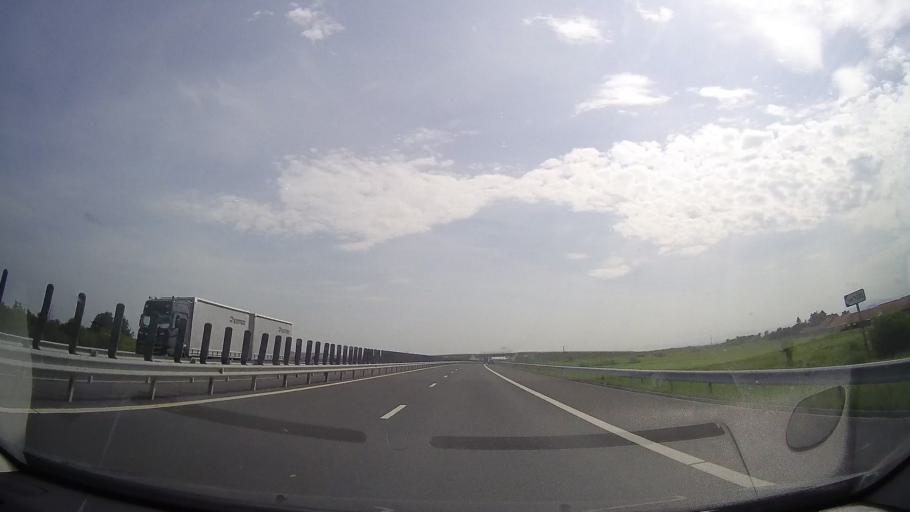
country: RO
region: Timis
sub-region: Comuna Bethausen
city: Bethausen
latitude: 45.8139
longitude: 21.9531
